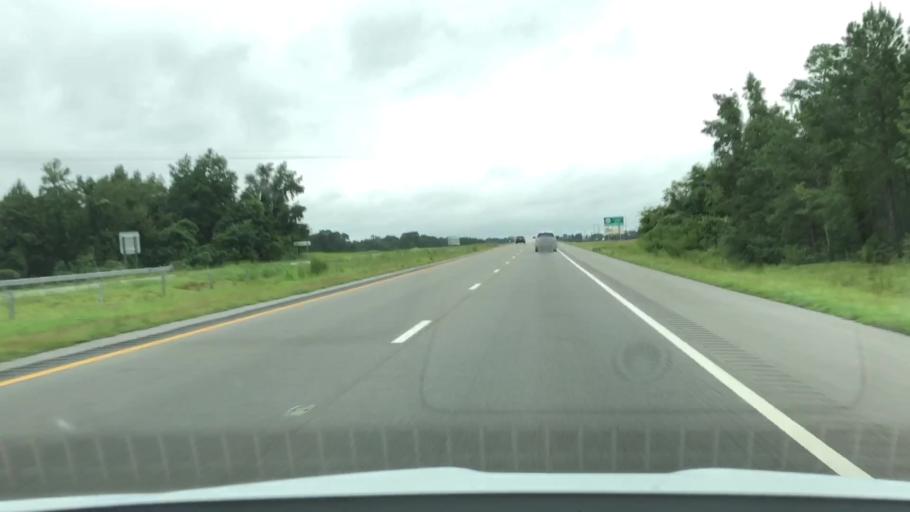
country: US
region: North Carolina
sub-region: Lenoir County
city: La Grange
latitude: 35.3115
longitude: -77.8250
